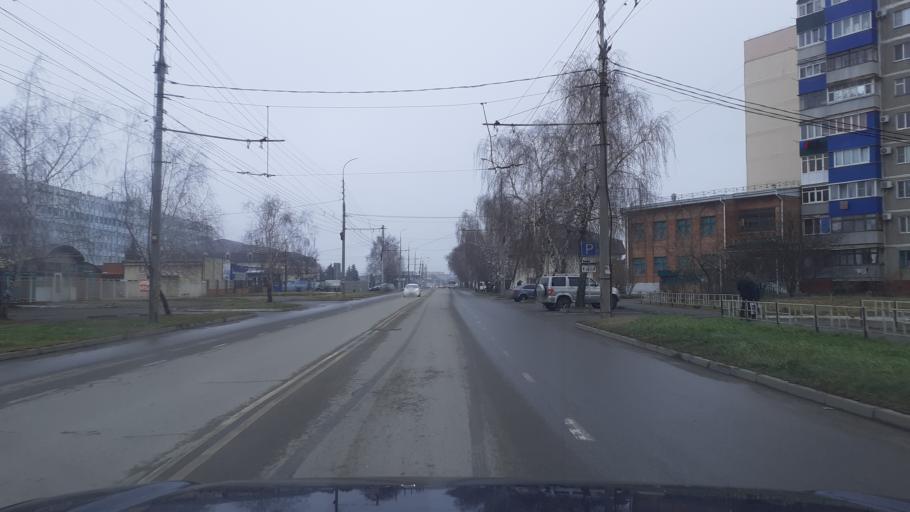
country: RU
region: Adygeya
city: Maykop
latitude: 44.6227
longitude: 40.0689
